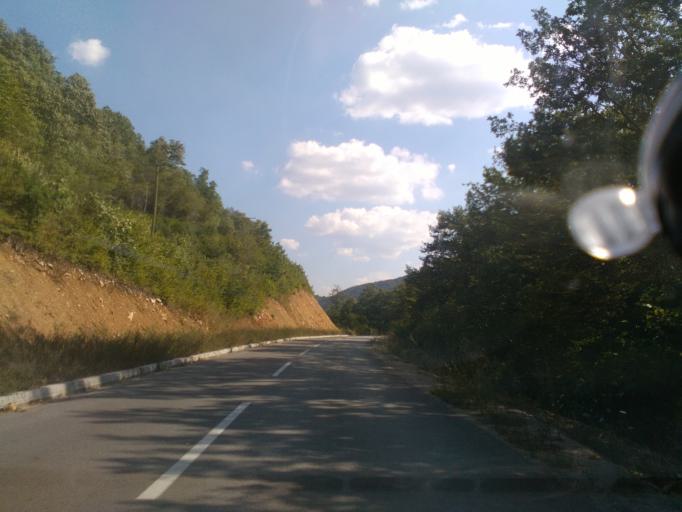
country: BA
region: Federation of Bosnia and Herzegovina
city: Orasac
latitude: 44.5046
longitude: 16.1298
